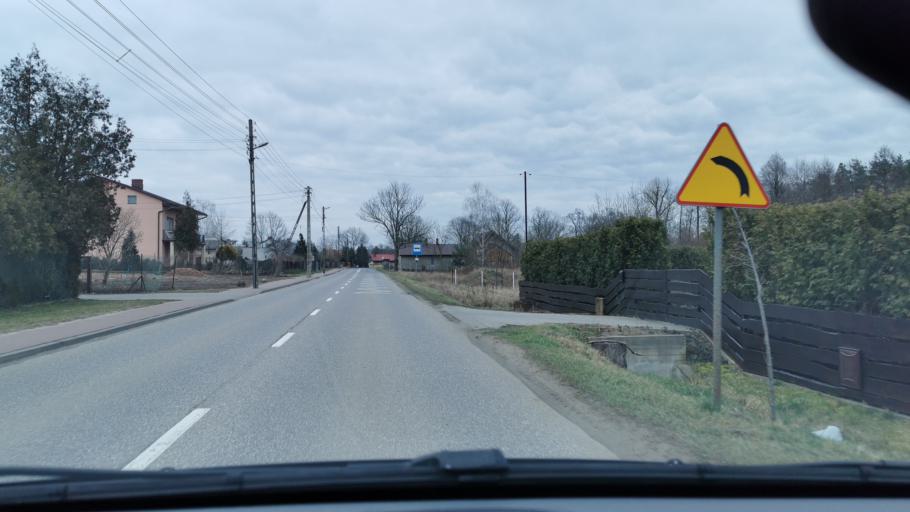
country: PL
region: Masovian Voivodeship
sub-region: Powiat zyrardowski
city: Radziejowice
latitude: 52.0104
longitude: 20.5295
